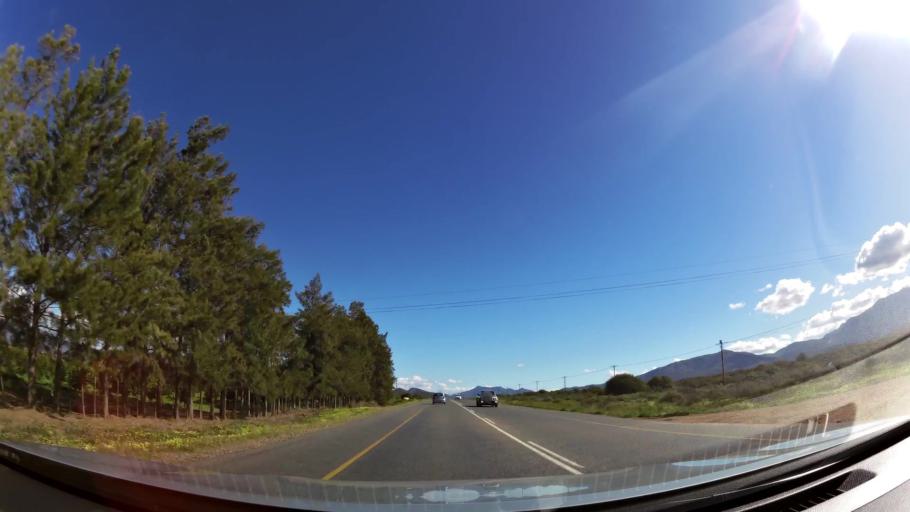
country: ZA
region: Western Cape
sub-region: Cape Winelands District Municipality
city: Ashton
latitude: -33.8144
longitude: 19.9234
